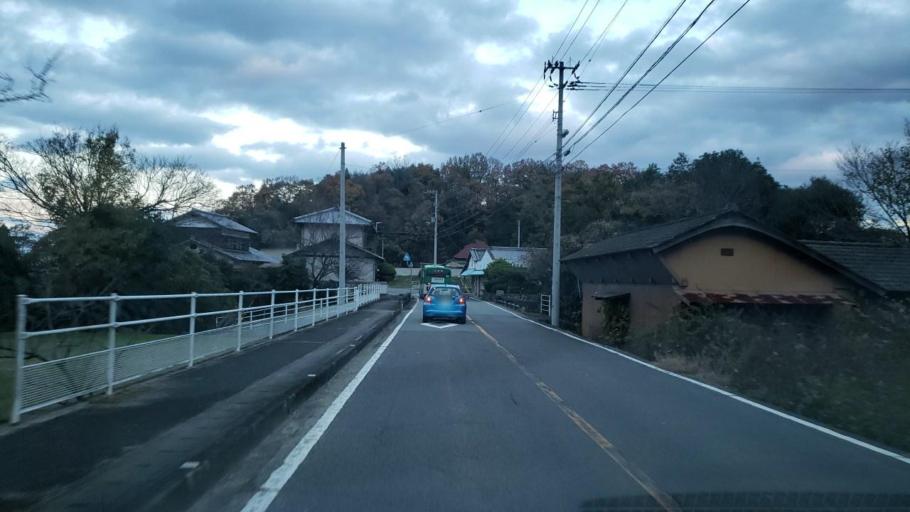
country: JP
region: Tokushima
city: Kamojimacho-jogejima
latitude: 34.2052
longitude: 134.3254
